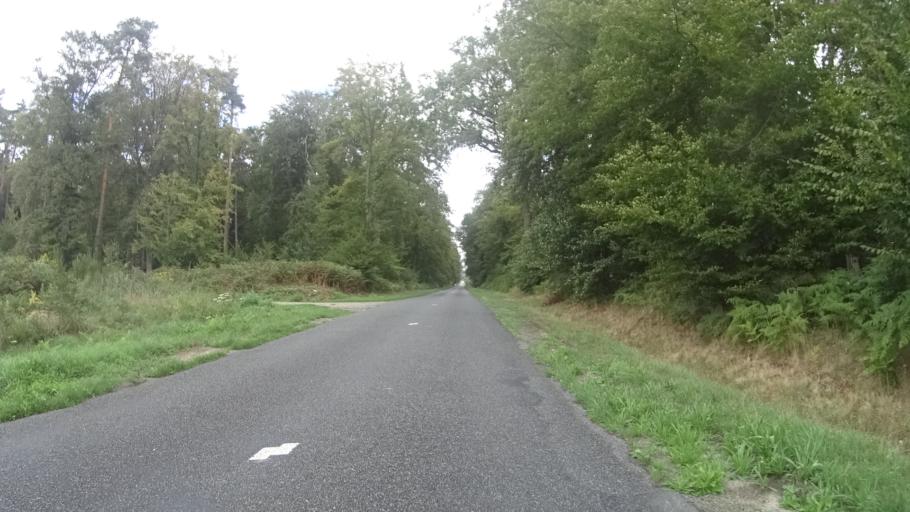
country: FR
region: Picardie
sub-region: Departement de l'Oise
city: Chiry-Ourscamp
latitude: 49.5460
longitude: 2.9845
